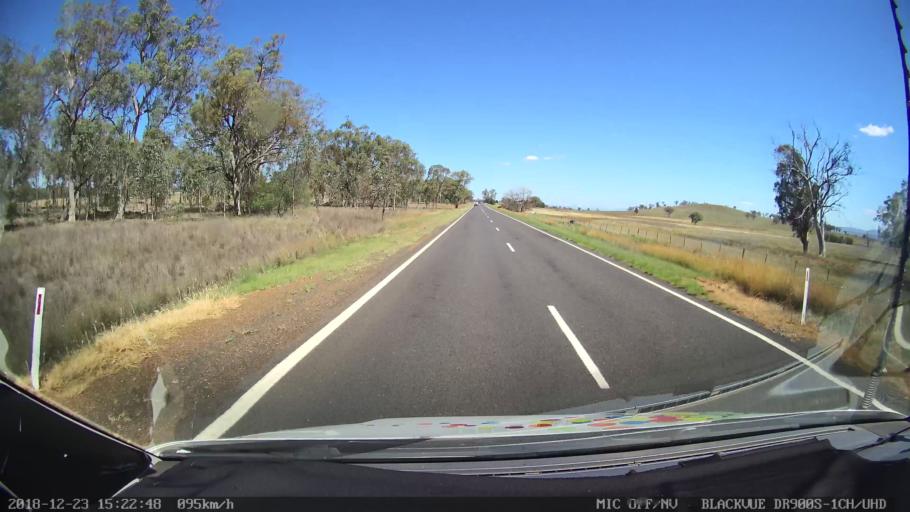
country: AU
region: New South Wales
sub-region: Tamworth Municipality
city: Manilla
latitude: -30.8727
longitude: 150.8083
